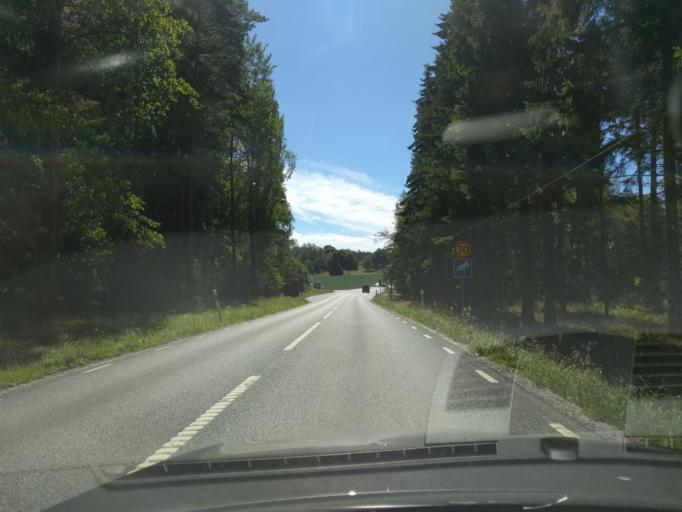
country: SE
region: Stockholm
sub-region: Haninge Kommun
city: Haninge
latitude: 59.1418
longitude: 18.1843
